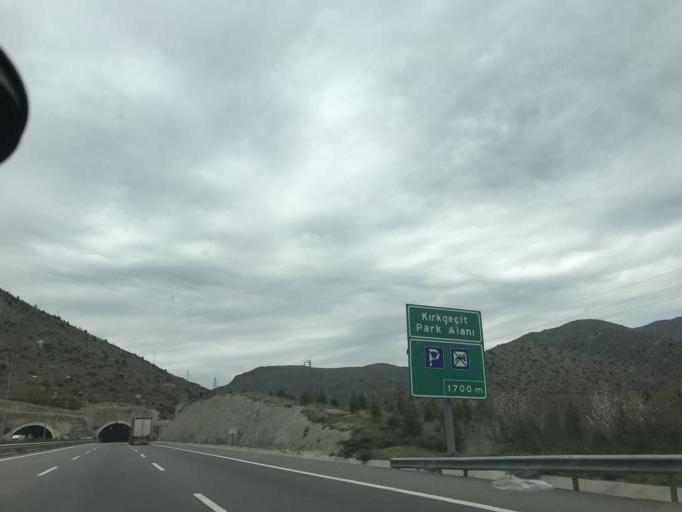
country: TR
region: Nigde
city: Ciftehan
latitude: 37.5722
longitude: 34.7536
